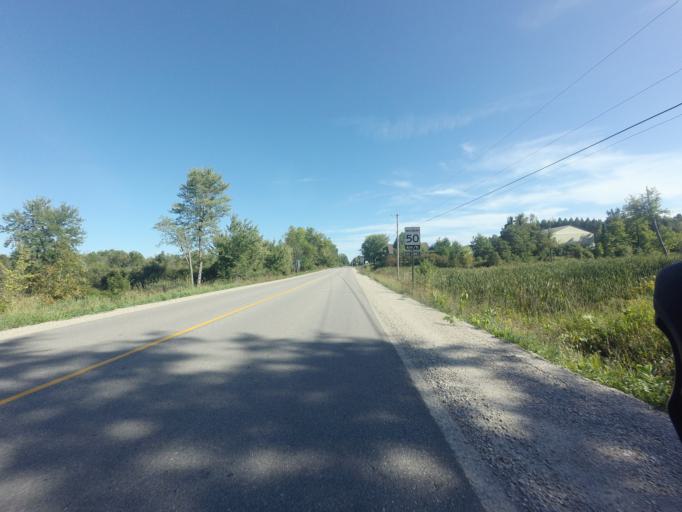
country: CA
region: Ontario
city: Perth
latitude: 44.8900
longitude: -76.3182
